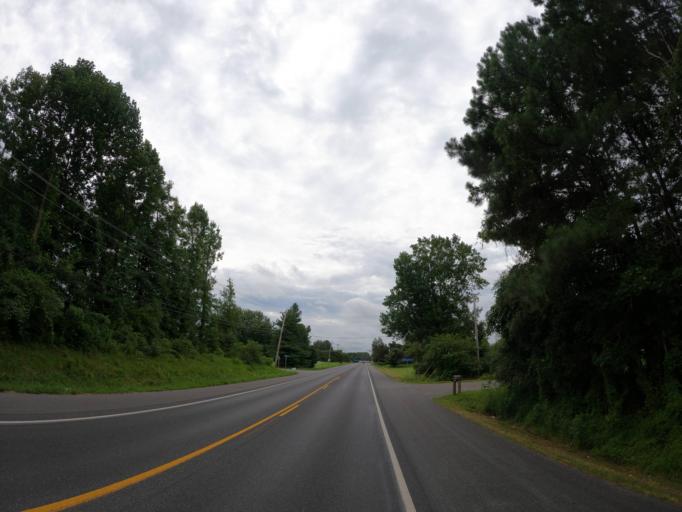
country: US
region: Maryland
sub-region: Saint Mary's County
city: California
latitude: 38.2293
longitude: -76.5191
